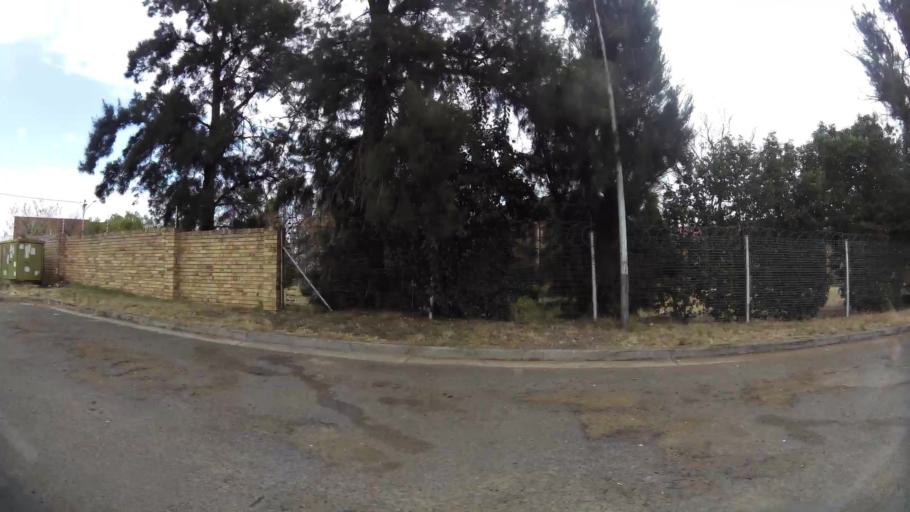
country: ZA
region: Orange Free State
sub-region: Fezile Dabi District Municipality
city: Kroonstad
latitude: -27.6472
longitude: 27.2338
